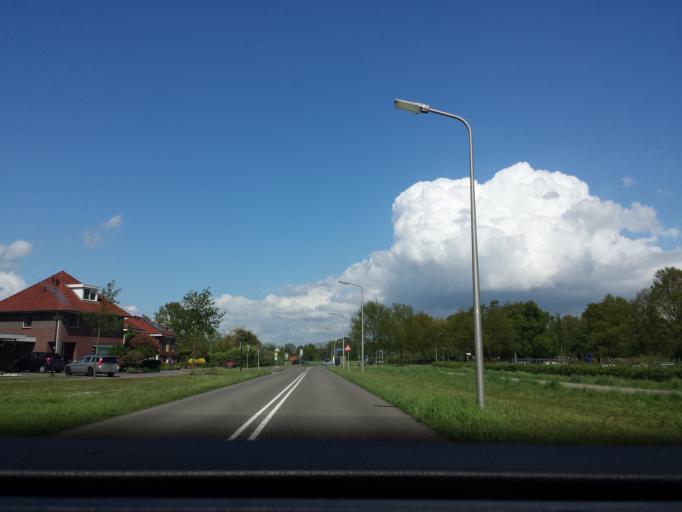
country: NL
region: Gelderland
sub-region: Gemeente Lochem
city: Barchem
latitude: 52.0893
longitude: 6.4585
